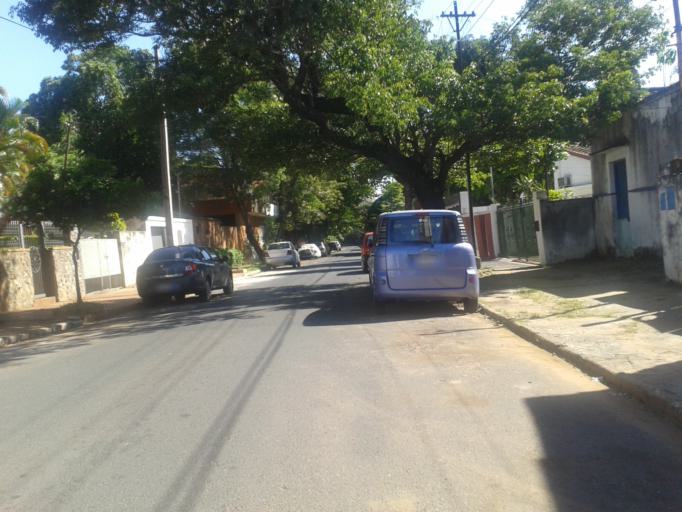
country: PY
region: Asuncion
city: Asuncion
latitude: -25.2947
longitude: -57.6364
